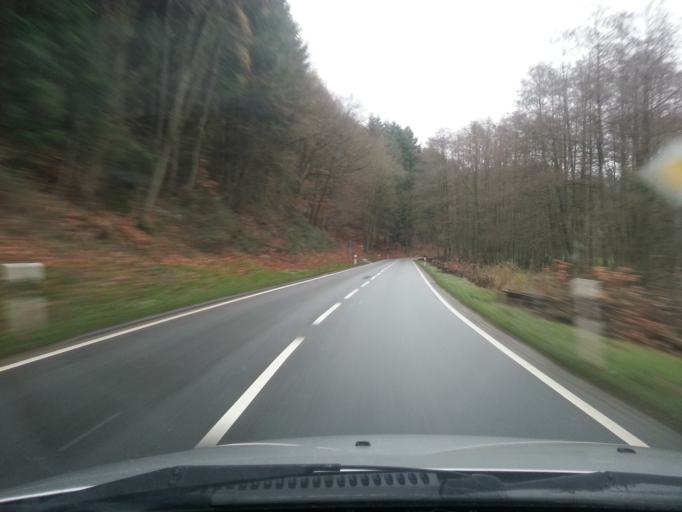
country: DE
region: Hesse
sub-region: Regierungsbezirk Darmstadt
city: Morlenbach
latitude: 49.5787
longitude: 8.7777
